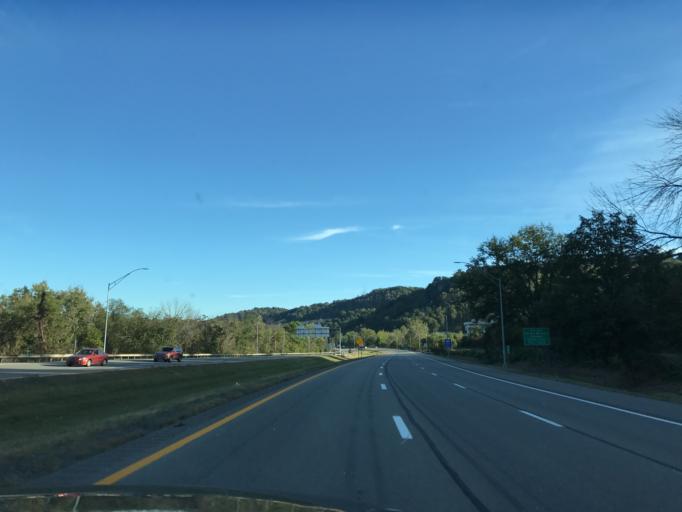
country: US
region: West Virginia
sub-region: Ohio County
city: Bethlehem
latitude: 40.0641
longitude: -80.6850
